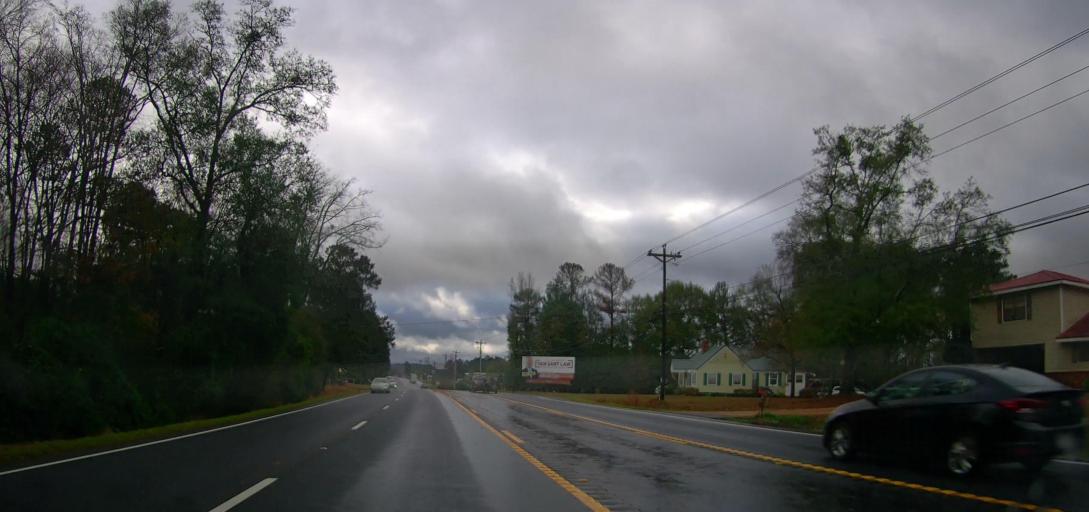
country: US
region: Georgia
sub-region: Clarke County
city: Country Club Estates
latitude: 34.0025
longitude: -83.3852
